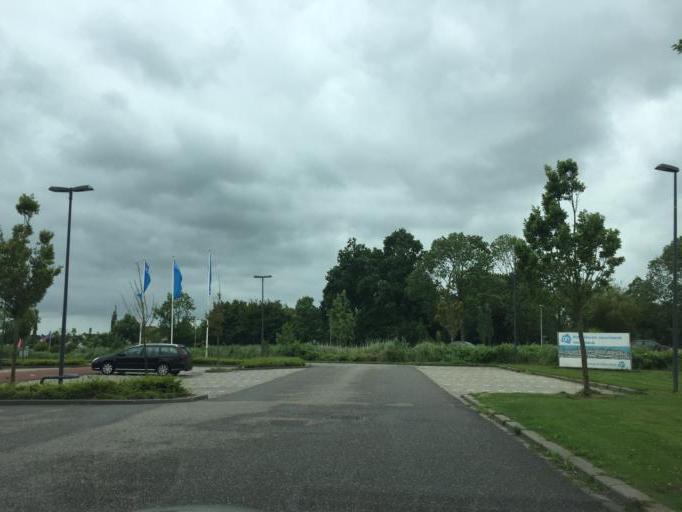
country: NL
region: Friesland
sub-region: Gemeente Dongeradeel
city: Dokkum
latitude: 53.3233
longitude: 6.0081
